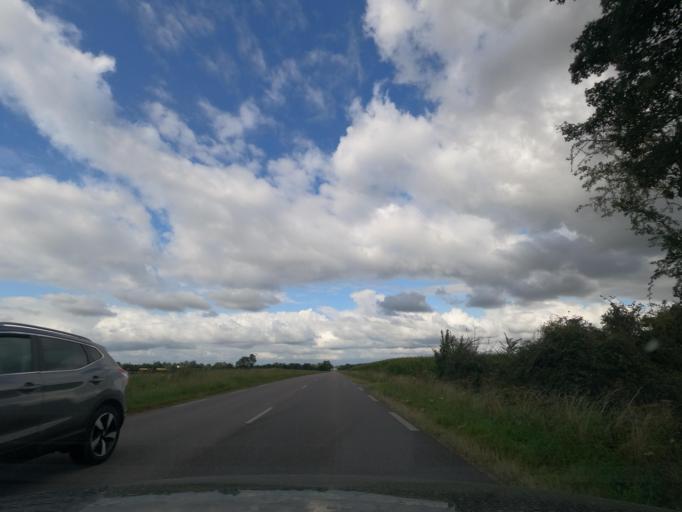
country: FR
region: Haute-Normandie
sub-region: Departement de l'Eure
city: Broglie
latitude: 48.9659
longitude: 0.4770
